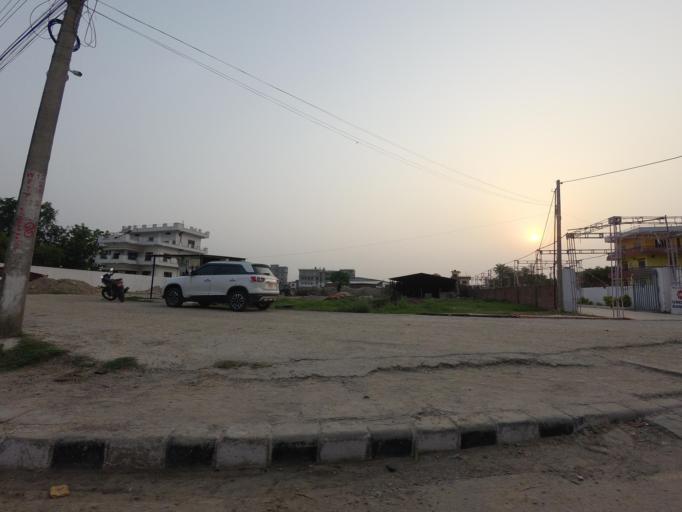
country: NP
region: Western Region
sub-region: Lumbini Zone
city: Bhairahawa
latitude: 27.5103
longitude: 83.4633
